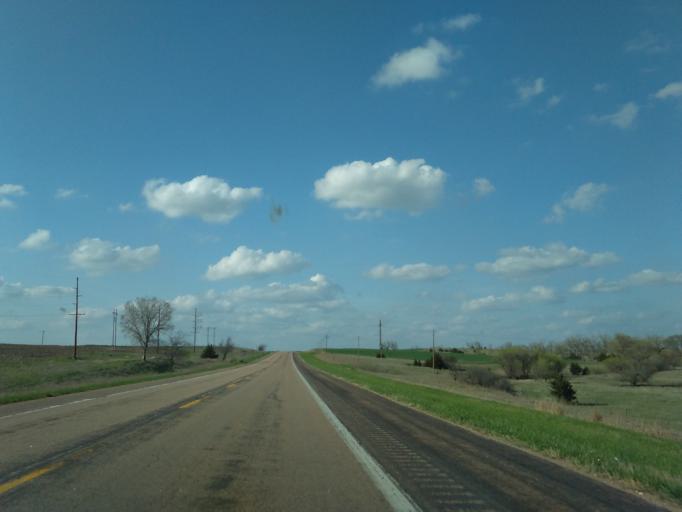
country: US
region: Nebraska
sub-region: Webster County
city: Red Cloud
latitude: 40.1148
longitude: -98.5189
